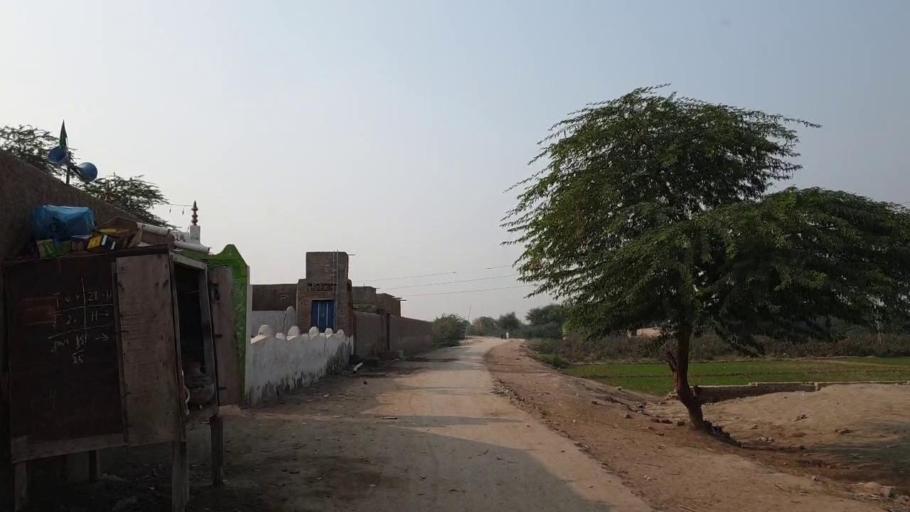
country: PK
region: Sindh
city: Bhan
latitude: 26.5584
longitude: 67.7112
